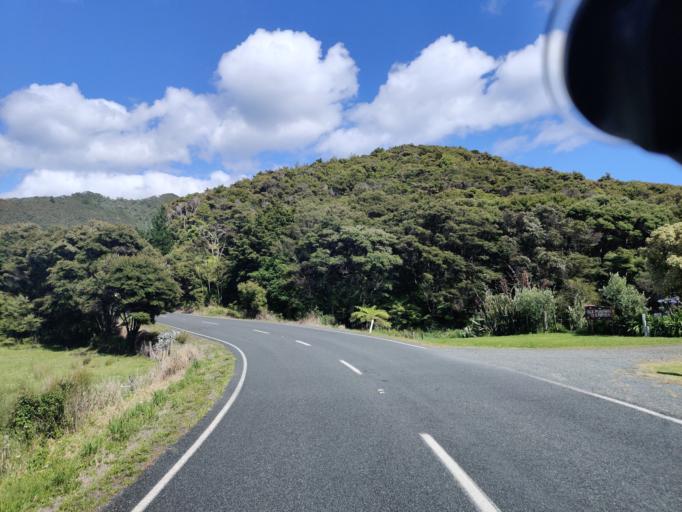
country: NZ
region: Northland
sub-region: Far North District
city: Paihia
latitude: -35.2689
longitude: 174.2753
